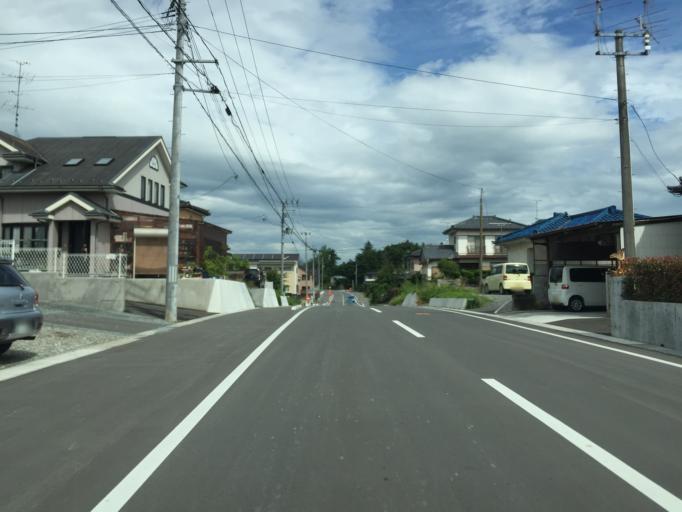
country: JP
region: Miyagi
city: Marumori
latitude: 37.8167
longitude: 140.9502
